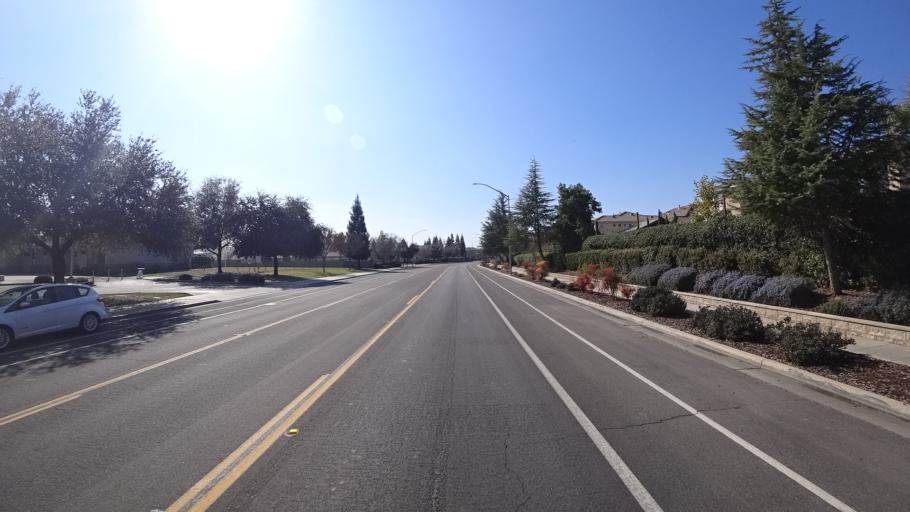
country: US
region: California
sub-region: Fresno County
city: Clovis
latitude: 36.8791
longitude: -119.7388
